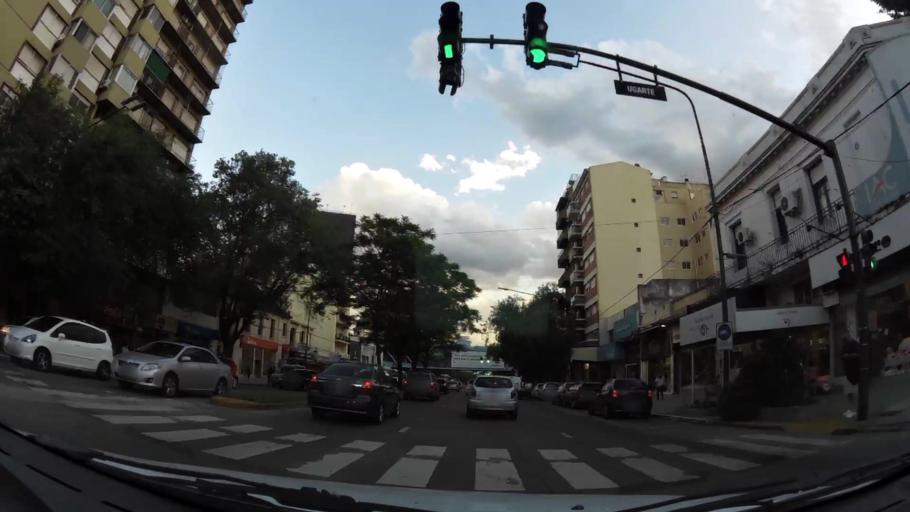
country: AR
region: Buenos Aires
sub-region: Partido de Vicente Lopez
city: Olivos
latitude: -34.5132
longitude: -58.4893
